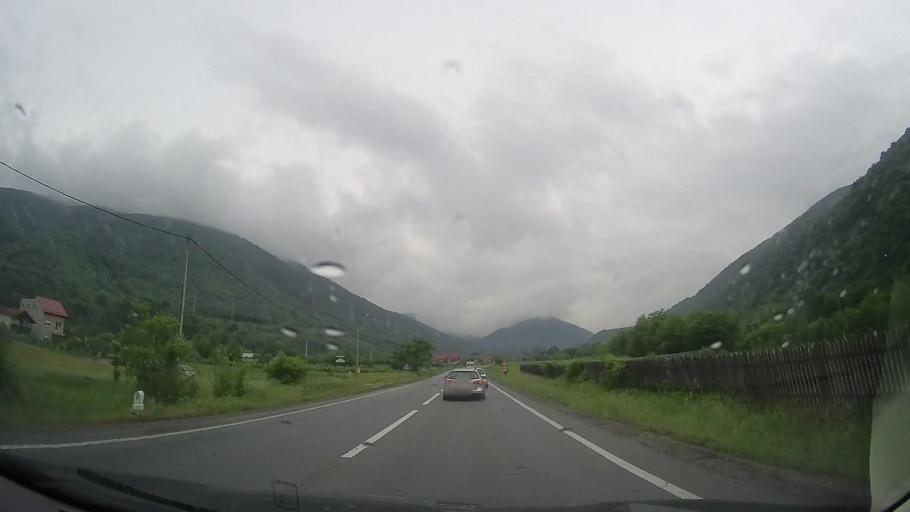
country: RO
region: Caras-Severin
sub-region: Comuna Mehadia
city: Mehadia
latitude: 44.8848
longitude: 22.3824
